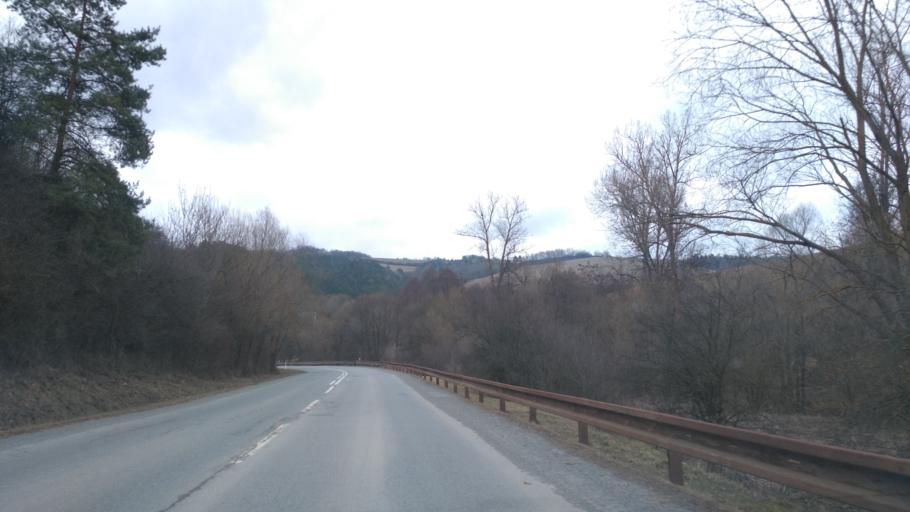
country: SK
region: Presovsky
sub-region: Okres Presov
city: Presov
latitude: 48.9596
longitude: 21.1130
